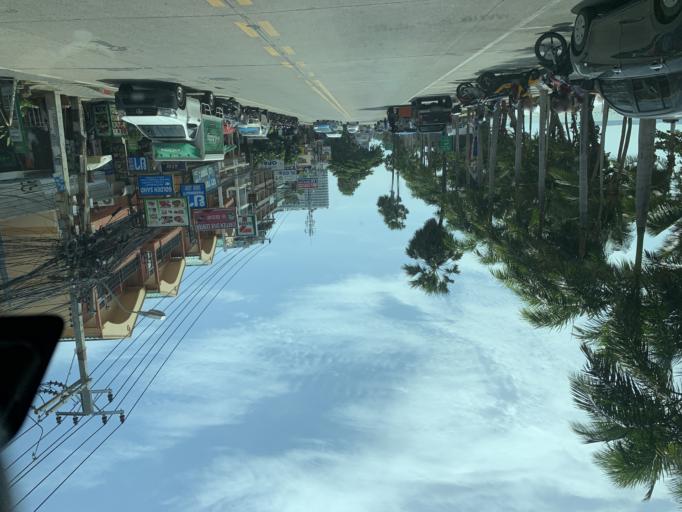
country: TH
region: Chon Buri
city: Phatthaya
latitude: 12.8952
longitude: 100.8704
